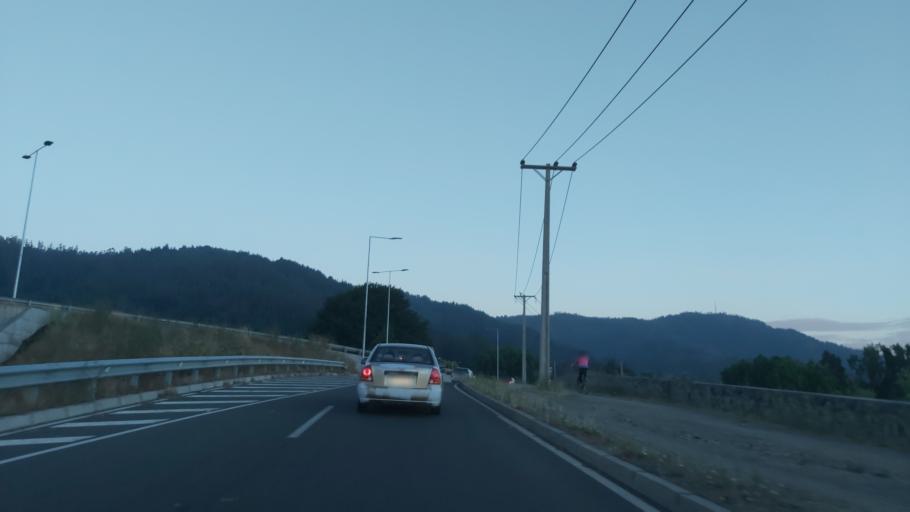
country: CL
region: Biobio
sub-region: Provincia de Concepcion
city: Chiguayante
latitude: -36.8949
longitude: -73.0351
